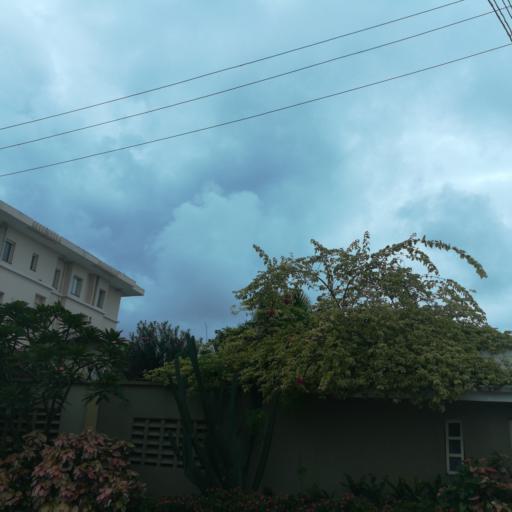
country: NG
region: Lagos
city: Ikoyi
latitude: 6.4467
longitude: 3.4572
